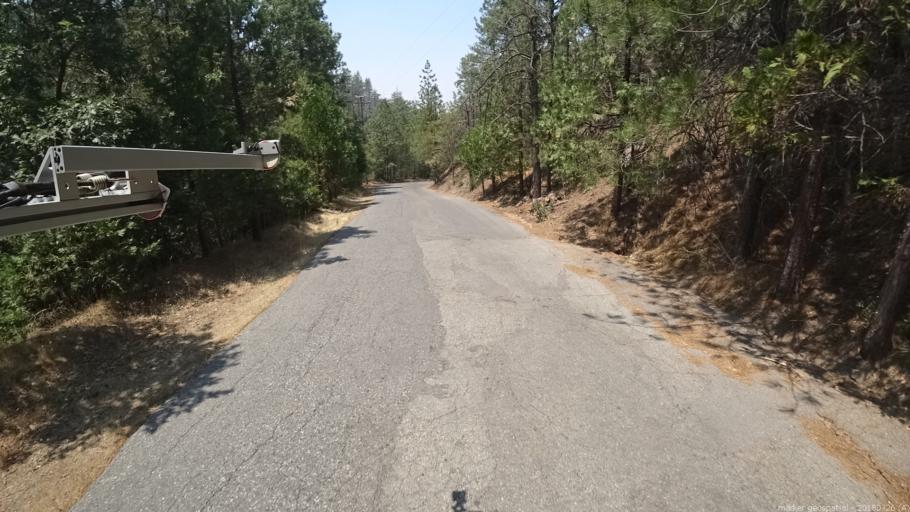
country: US
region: California
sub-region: Madera County
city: Oakhurst
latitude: 37.2771
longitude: -119.6283
